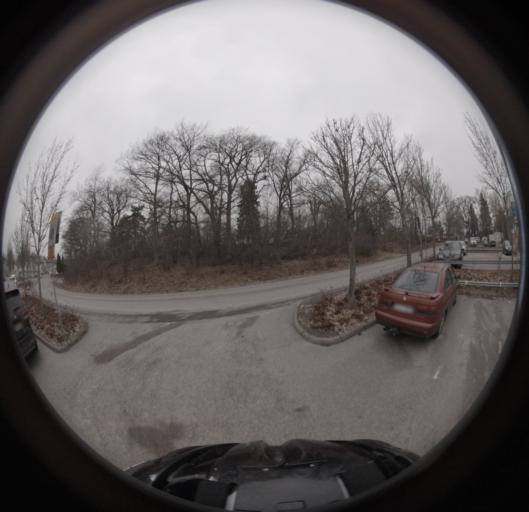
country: SE
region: Stockholm
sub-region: Upplands Vasby Kommun
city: Upplands Vaesby
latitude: 59.4847
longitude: 17.9340
